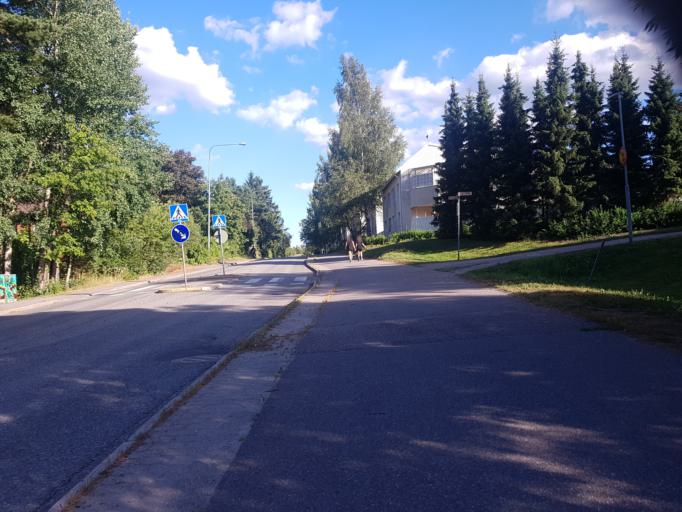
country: FI
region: Uusimaa
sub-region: Helsinki
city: Vantaa
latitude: 60.2712
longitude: 25.0058
